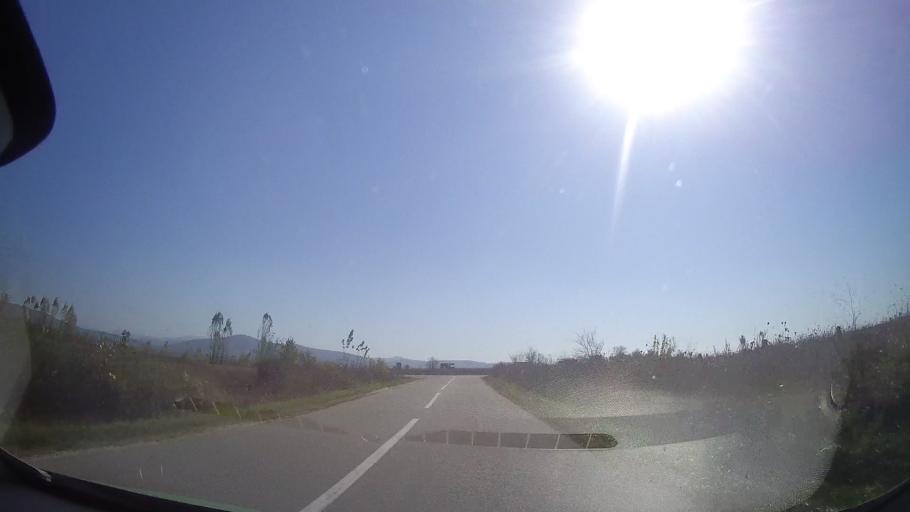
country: RO
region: Timis
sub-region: Comuna Traian Vuia
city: Traian Vuia
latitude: 45.7794
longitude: 22.0514
